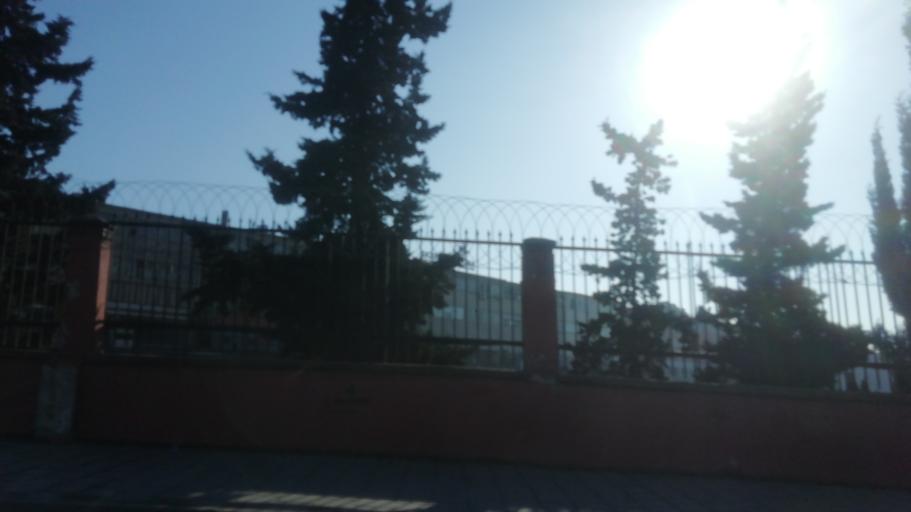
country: TR
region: Istanbul
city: Basaksehir
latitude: 41.1002
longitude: 28.7926
